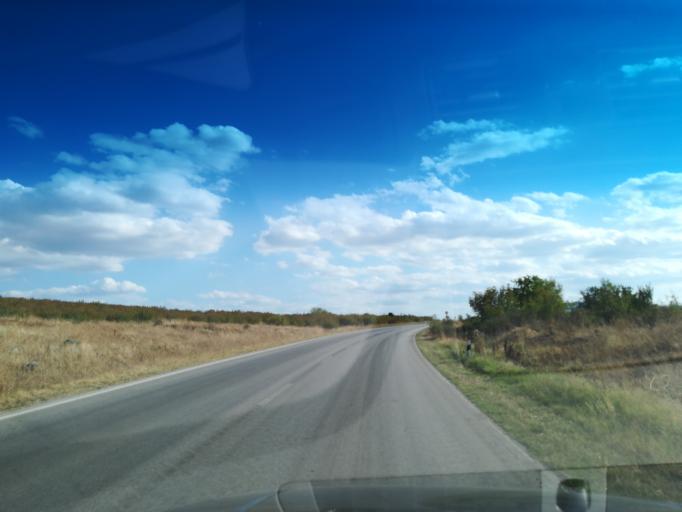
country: BG
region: Khaskovo
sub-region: Obshtina Mineralni Bani
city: Mineralni Bani
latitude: 41.9764
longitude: 25.3528
